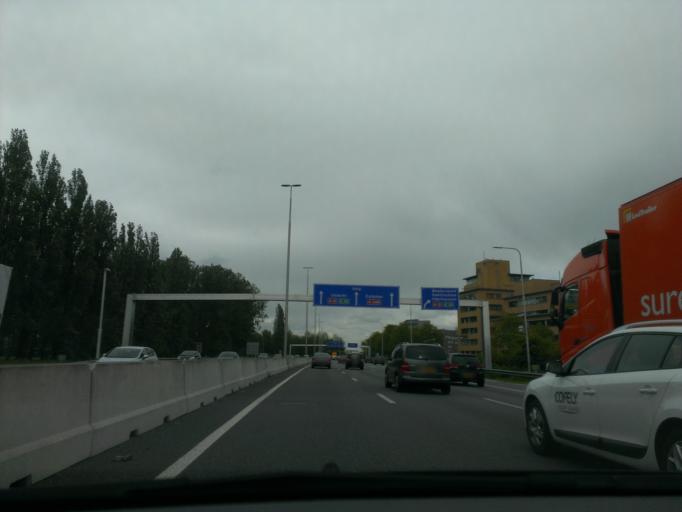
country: NL
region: Gelderland
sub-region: Gemeente Rheden
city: Velp
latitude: 51.9791
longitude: 5.9717
